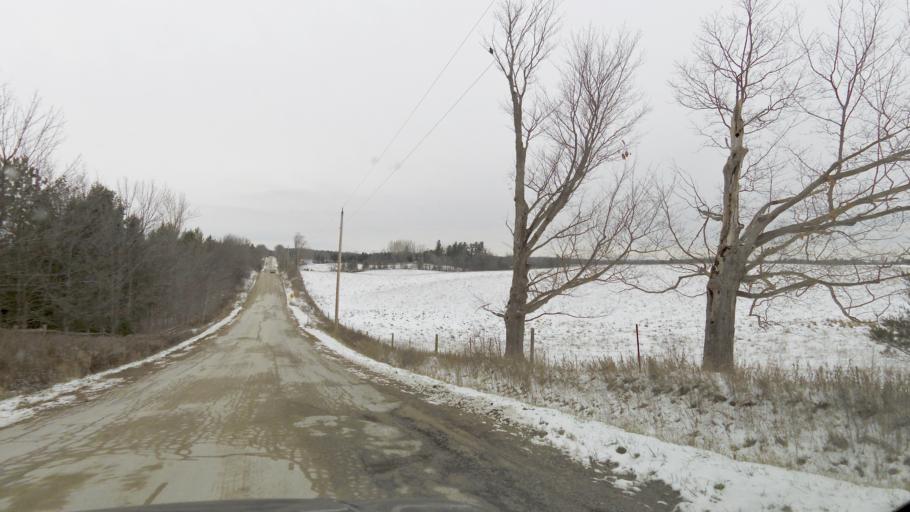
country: CA
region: Ontario
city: Vaughan
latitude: 43.9310
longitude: -79.6079
